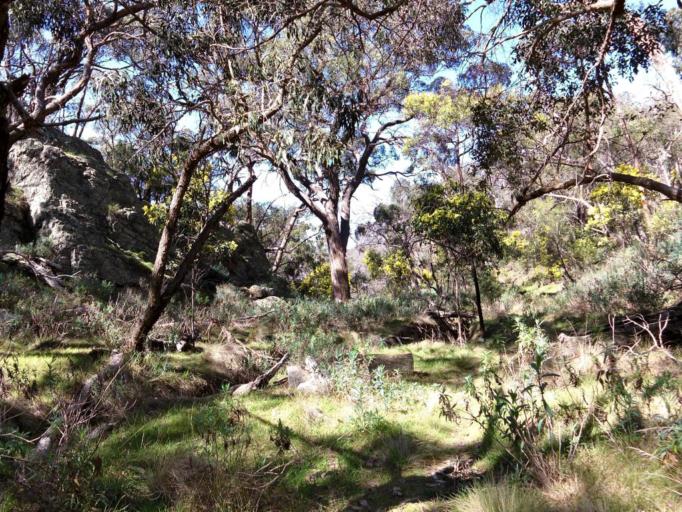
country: AU
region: Victoria
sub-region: Moorabool
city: Bacchus Marsh
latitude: -37.6623
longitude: 144.3225
